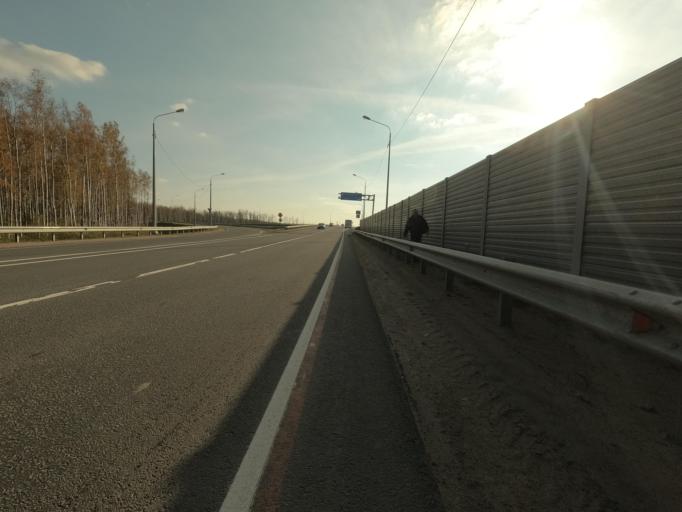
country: RU
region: Leningrad
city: Mga
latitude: 59.7602
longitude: 31.0936
